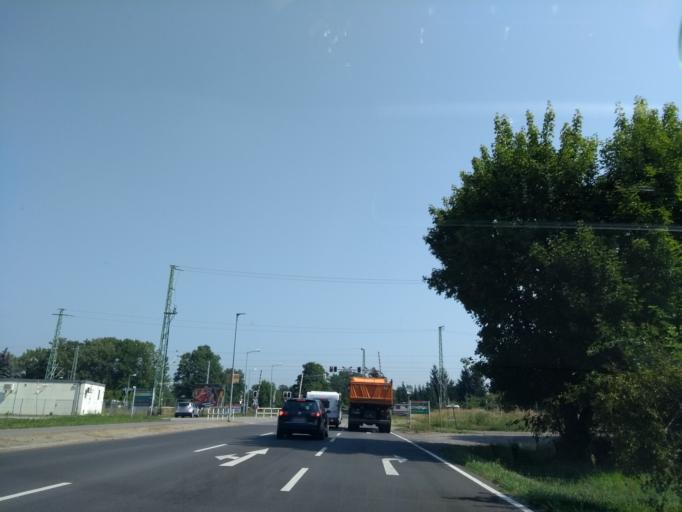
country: DE
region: Brandenburg
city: Lubbenau
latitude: 51.8588
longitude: 13.9662
